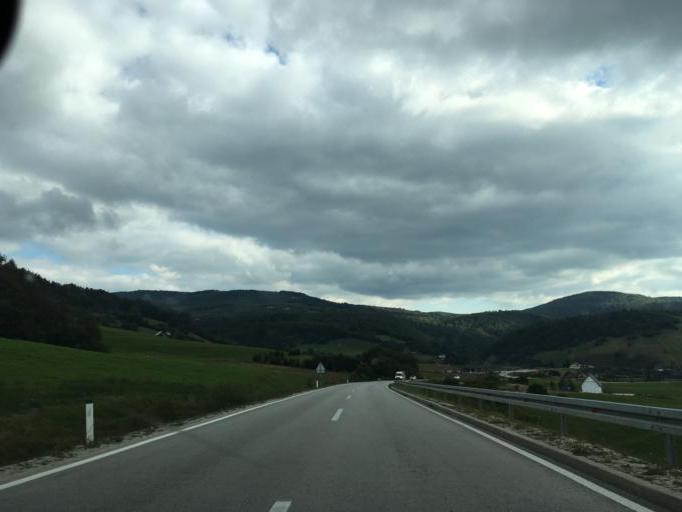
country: BA
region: Federation of Bosnia and Herzegovina
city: Novi Travnik
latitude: 44.1098
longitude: 17.5754
